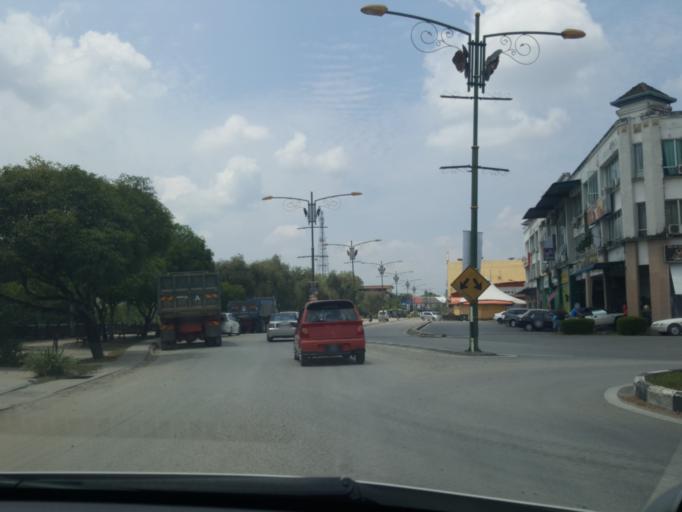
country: MY
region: Sarawak
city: Sarikei
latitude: 2.1328
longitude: 111.5250
